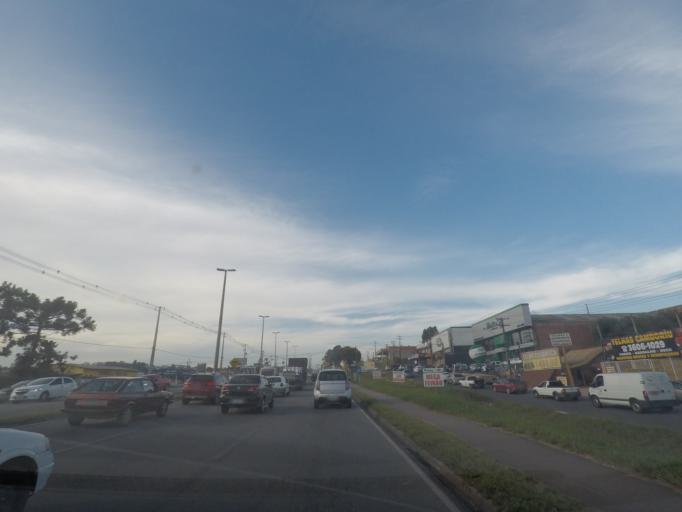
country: BR
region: Parana
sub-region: Pinhais
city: Pinhais
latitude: -25.3748
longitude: -49.1937
